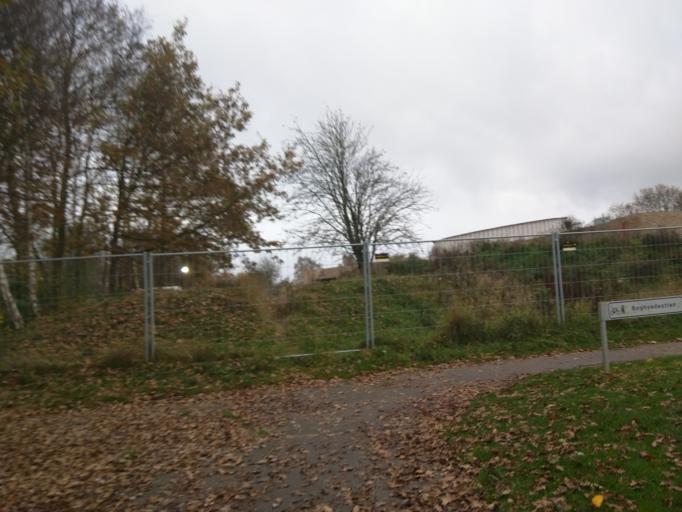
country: DK
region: Central Jutland
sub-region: Viborg Kommune
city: Viborg
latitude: 56.4642
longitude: 9.3893
